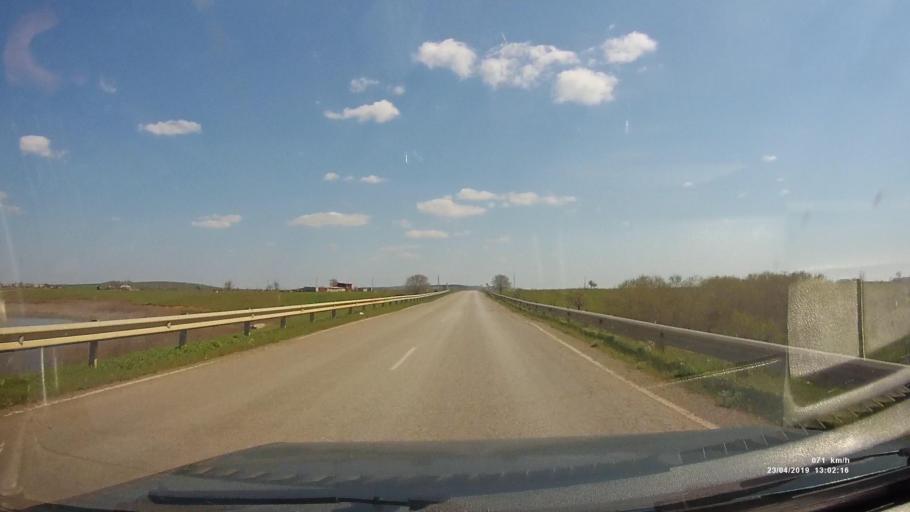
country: RU
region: Kalmykiya
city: Yashalta
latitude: 46.6012
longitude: 42.6670
